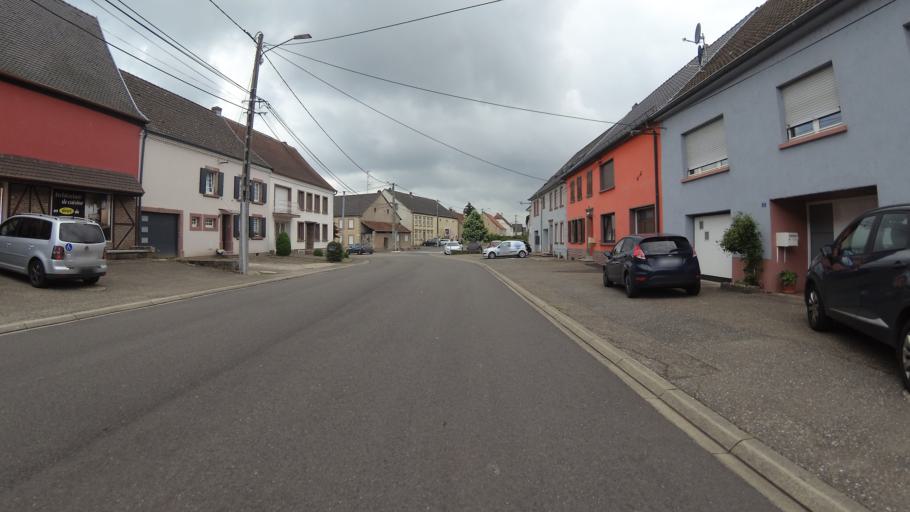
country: FR
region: Lorraine
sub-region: Departement de la Moselle
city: Remelfing
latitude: 49.0615
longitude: 7.0906
